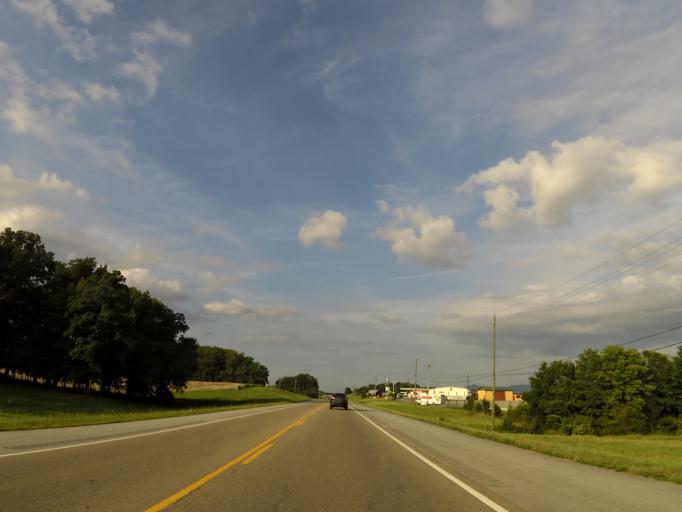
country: US
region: Tennessee
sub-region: Jefferson County
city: Dandridge
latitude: 35.9032
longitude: -83.4207
